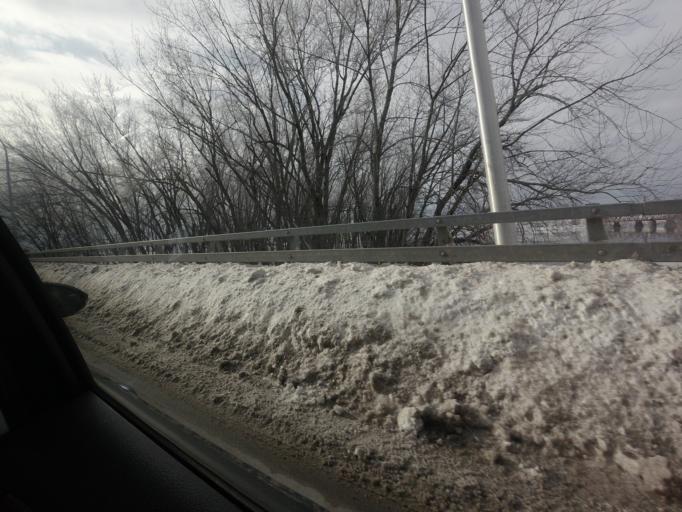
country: CA
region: New Brunswick
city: Fredericton
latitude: 45.9559
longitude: -66.6231
